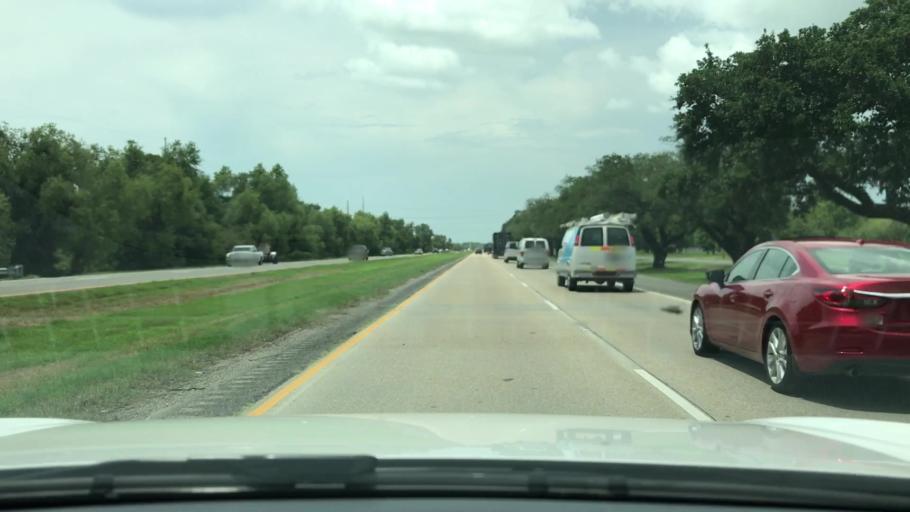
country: US
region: Louisiana
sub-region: West Baton Rouge Parish
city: Addis
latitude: 30.3258
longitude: -91.2540
